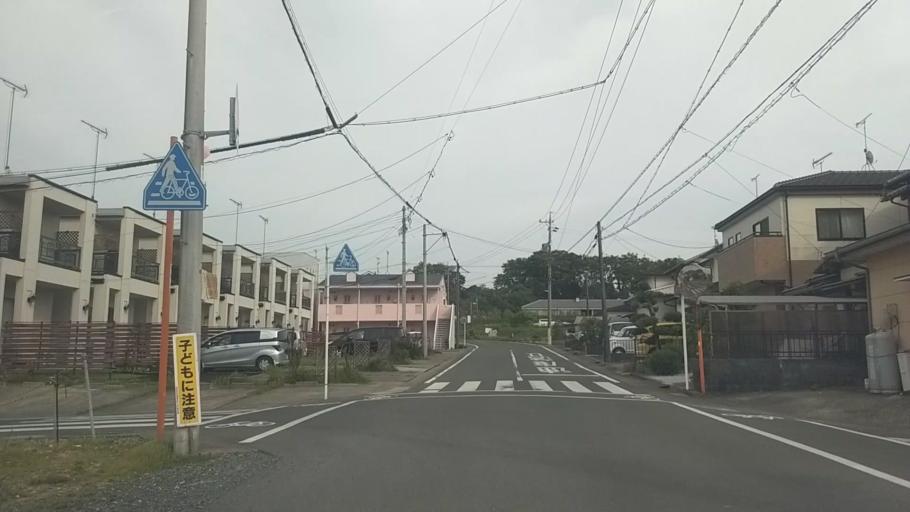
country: JP
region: Shizuoka
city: Kosai-shi
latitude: 34.7583
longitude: 137.6126
